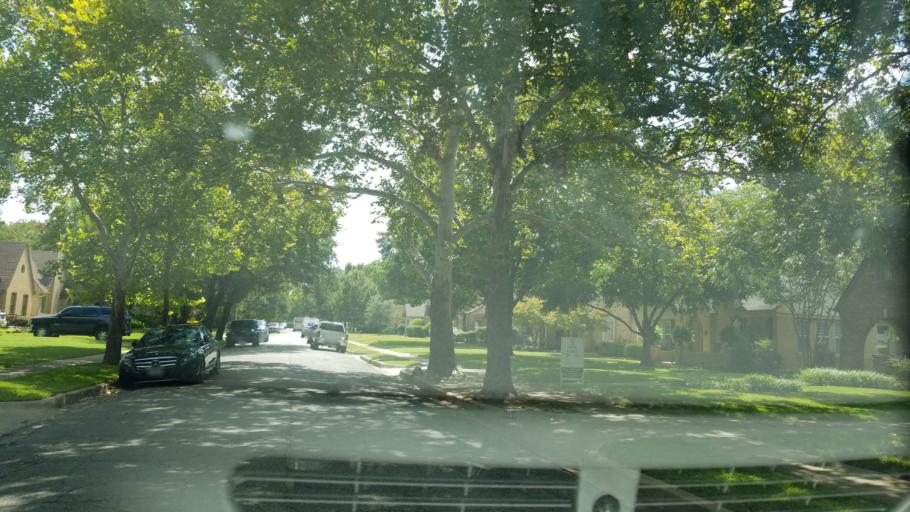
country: US
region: Texas
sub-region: Dallas County
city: Dallas
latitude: 32.7582
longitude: -96.8440
